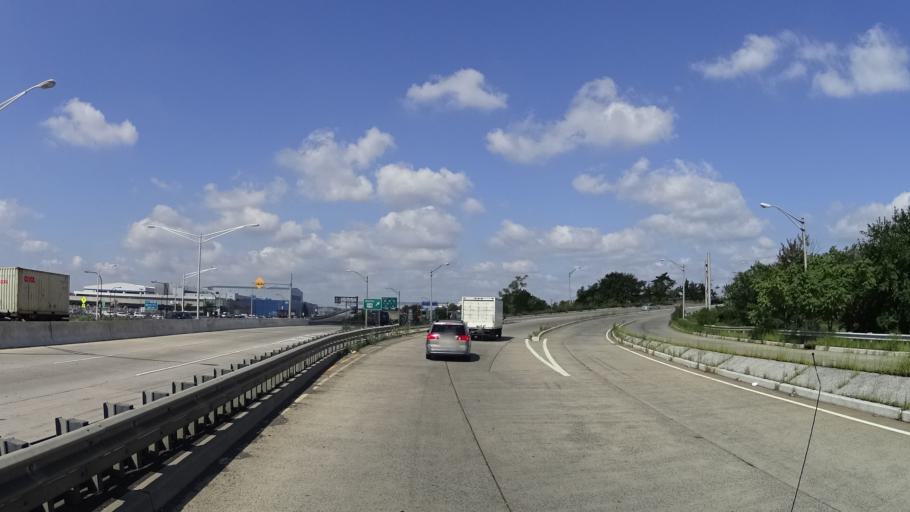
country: US
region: New Jersey
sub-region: Essex County
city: Newark
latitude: 40.7086
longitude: -74.1604
